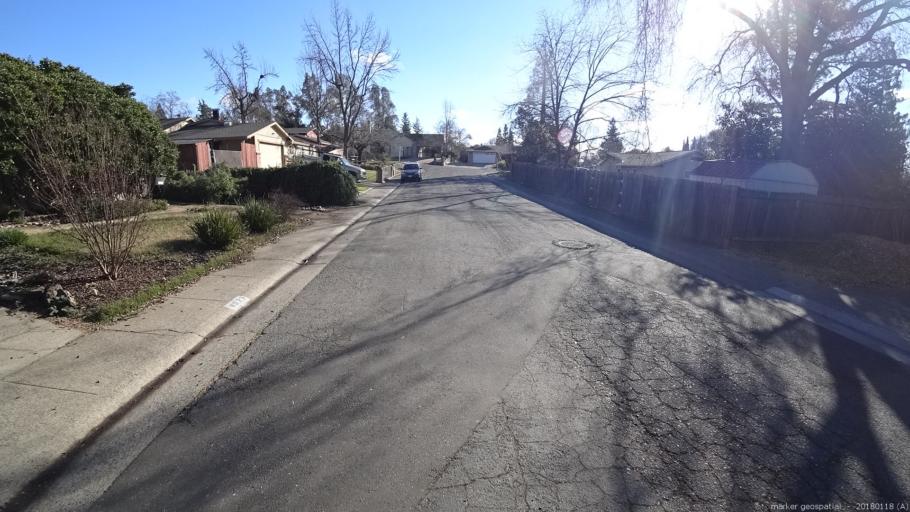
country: US
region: California
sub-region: Sacramento County
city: Orangevale
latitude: 38.6740
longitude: -121.2386
